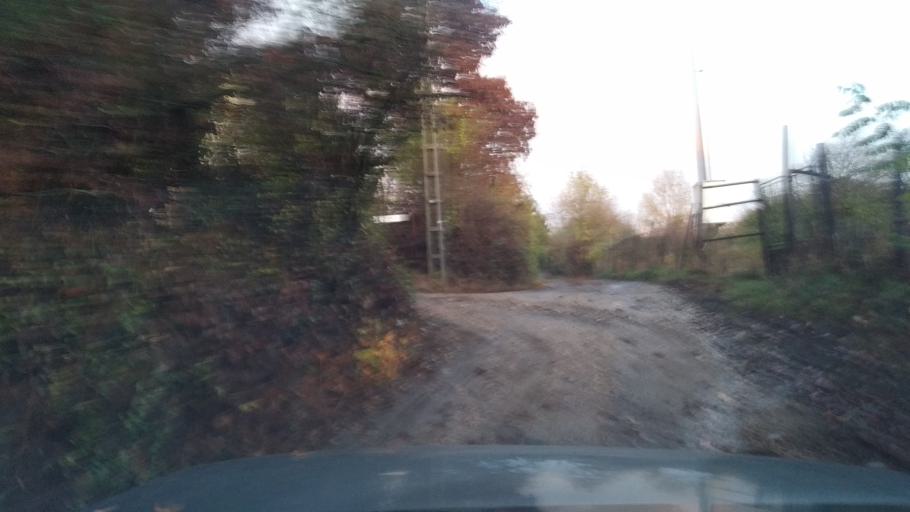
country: HU
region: Pest
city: Nagykovacsi
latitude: 47.6645
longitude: 18.9999
